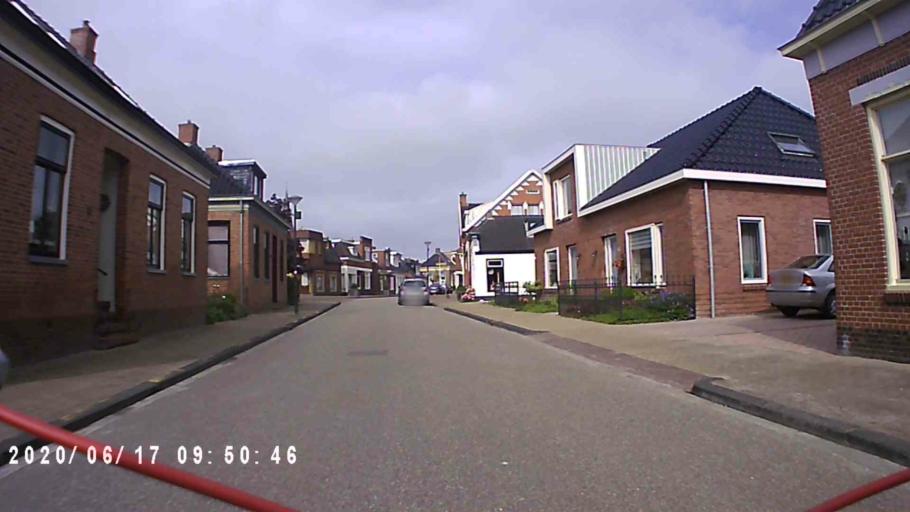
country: NL
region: Groningen
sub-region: Gemeente De Marne
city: Ulrum
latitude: 53.3593
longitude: 6.3339
